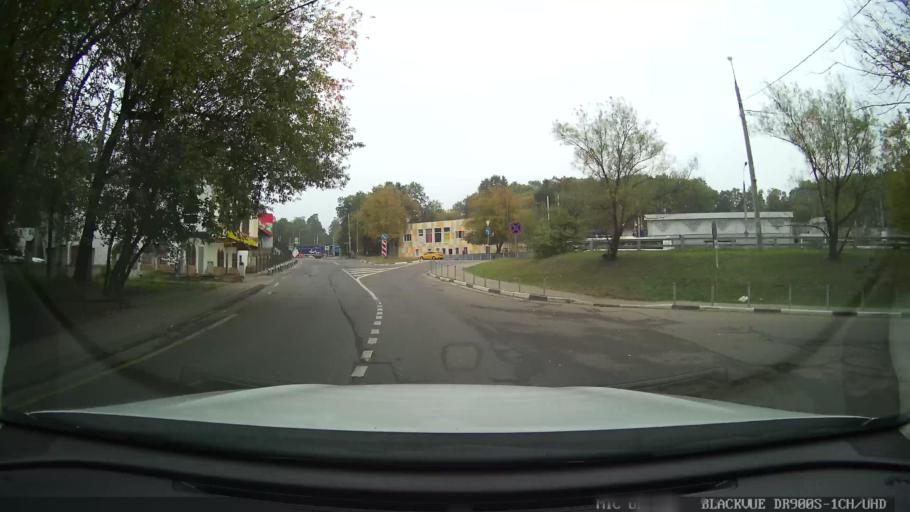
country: RU
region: Moscow
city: Novo-Peredelkino
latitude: 55.6552
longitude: 37.3535
